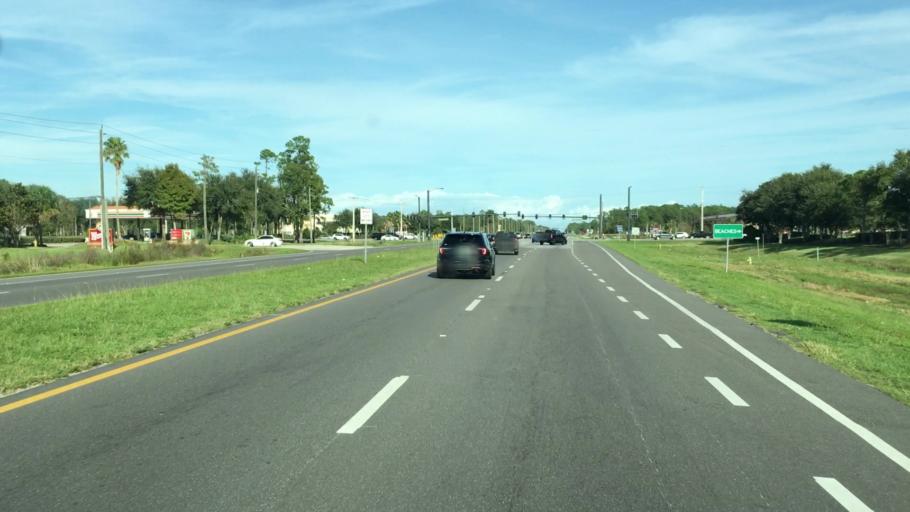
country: US
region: Florida
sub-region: Volusia County
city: Holly Hill
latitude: 29.2230
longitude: -81.0958
